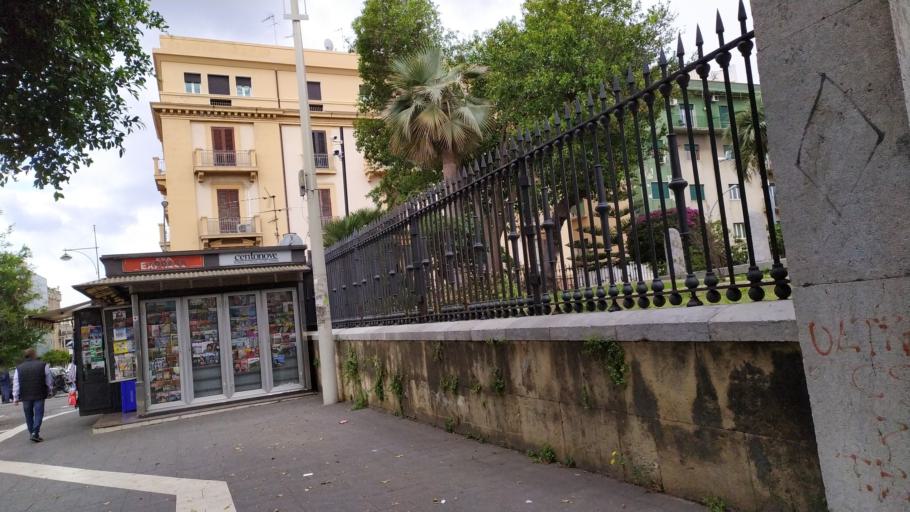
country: IT
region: Sicily
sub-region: Messina
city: Messina
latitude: 38.1883
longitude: 15.5532
